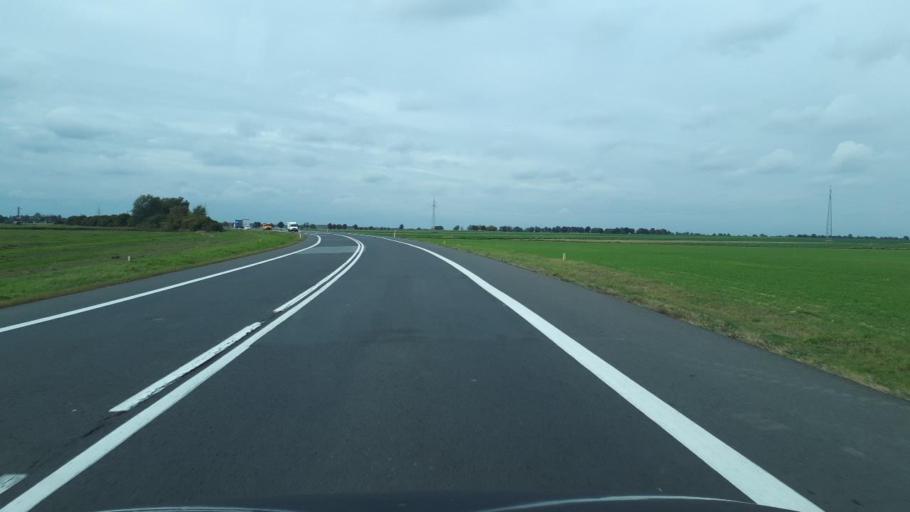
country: PL
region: Opole Voivodeship
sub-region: Powiat kluczborski
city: Kluczbork
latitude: 50.9878
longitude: 18.2360
